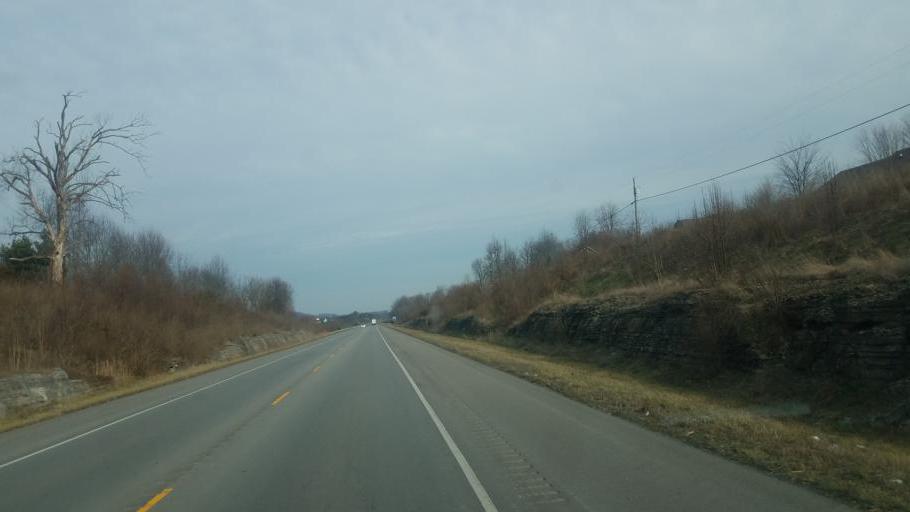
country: US
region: Kentucky
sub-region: Boyle County
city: Junction City
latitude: 37.5243
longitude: -84.8057
